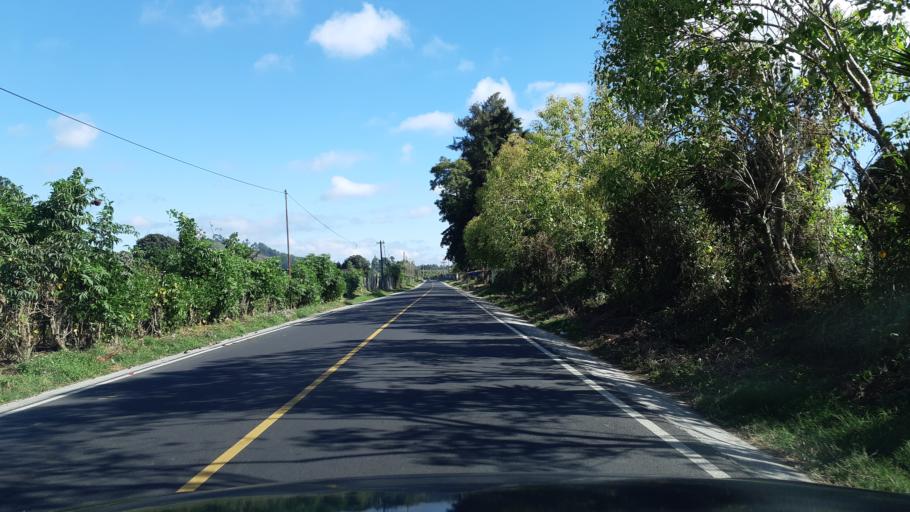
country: GT
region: Chimaltenango
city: San Andres Itzapa
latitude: 14.6349
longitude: -90.8272
